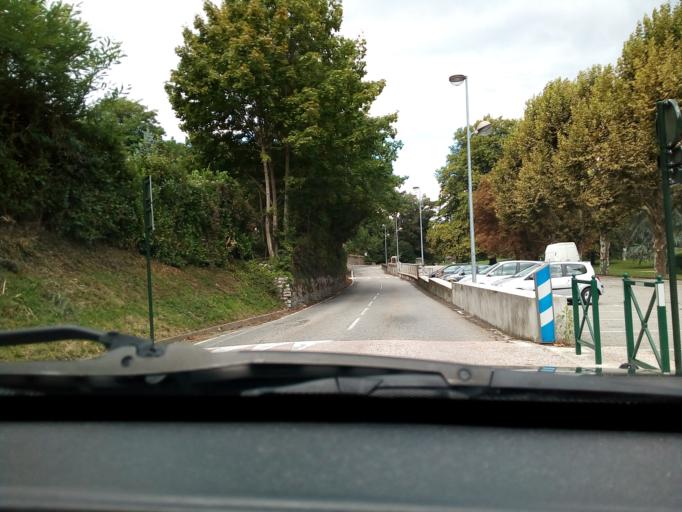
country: FR
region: Rhone-Alpes
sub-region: Departement de la Savoie
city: Chambery
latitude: 45.5599
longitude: 5.9386
